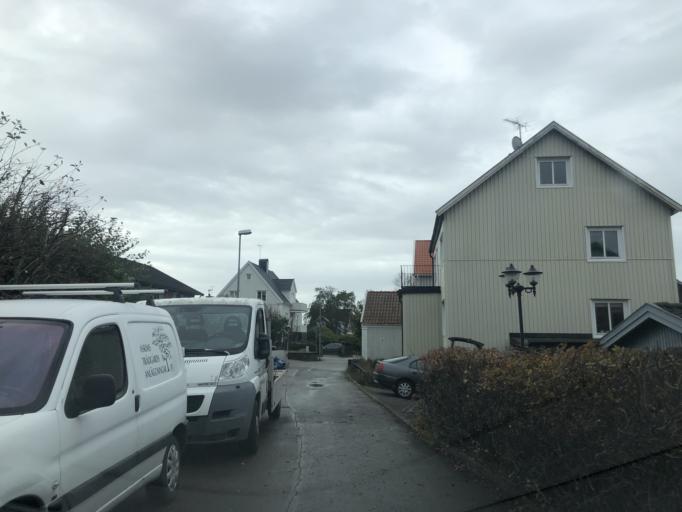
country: SE
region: Vaestra Goetaland
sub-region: Goteborg
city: Majorna
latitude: 57.6754
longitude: 11.8916
